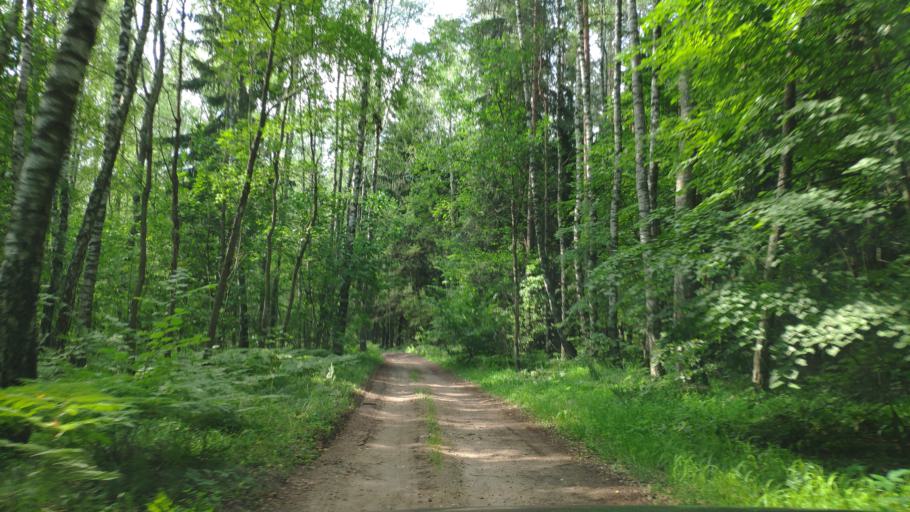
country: BY
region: Minsk
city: Zaslawye
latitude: 53.9713
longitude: 27.2935
